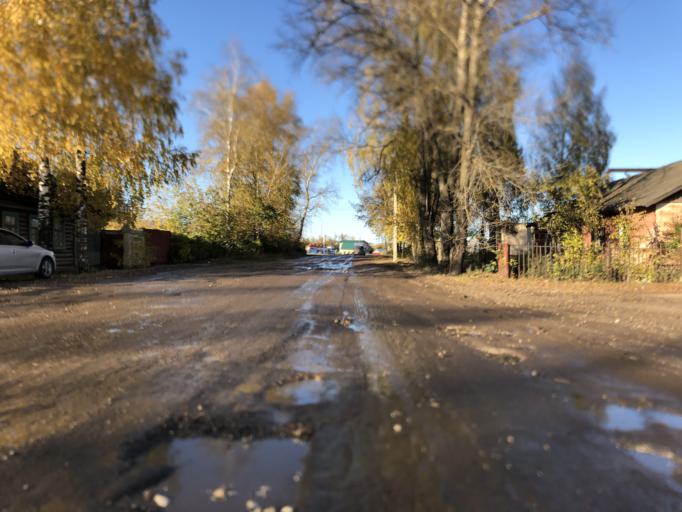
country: RU
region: Tverskaya
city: Rzhev
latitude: 56.2393
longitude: 34.3463
